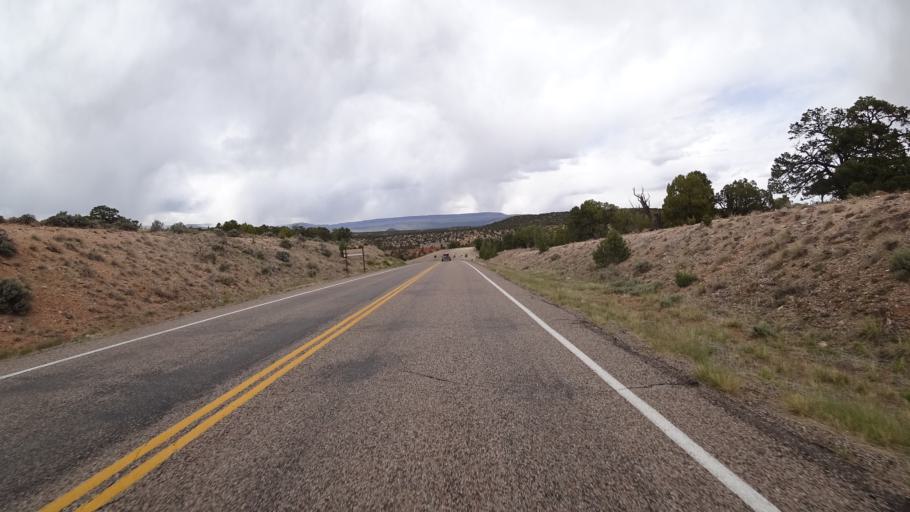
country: US
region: Utah
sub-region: Wayne County
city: Loa
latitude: 37.8890
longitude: -111.4579
